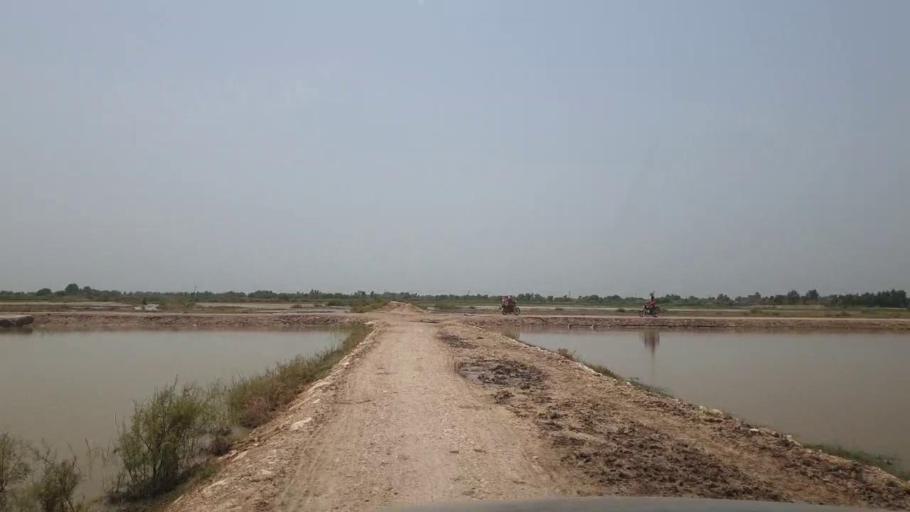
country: PK
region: Sindh
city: Garhi Yasin
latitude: 27.8579
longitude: 68.4765
